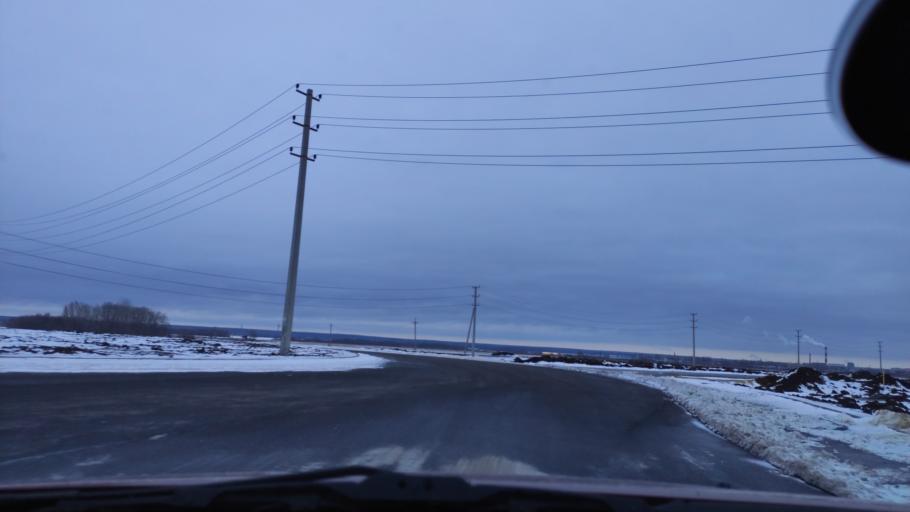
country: RU
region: Tambov
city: Donskoye
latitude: 52.7867
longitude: 41.4311
